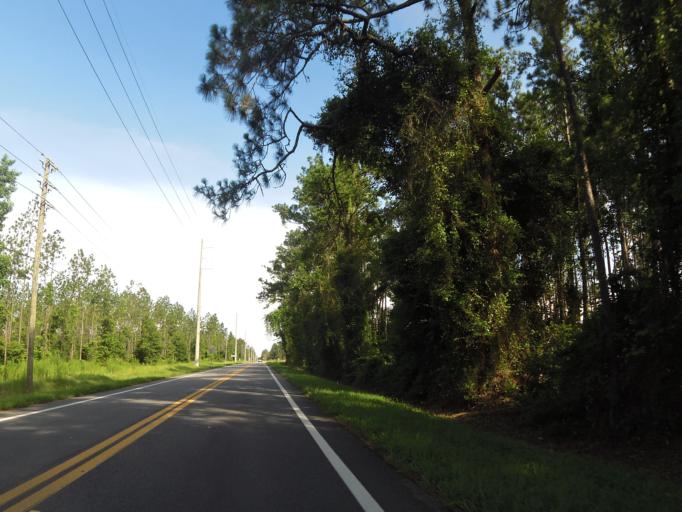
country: US
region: Florida
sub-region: Clay County
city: Green Cove Springs
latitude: 30.0090
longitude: -81.5541
